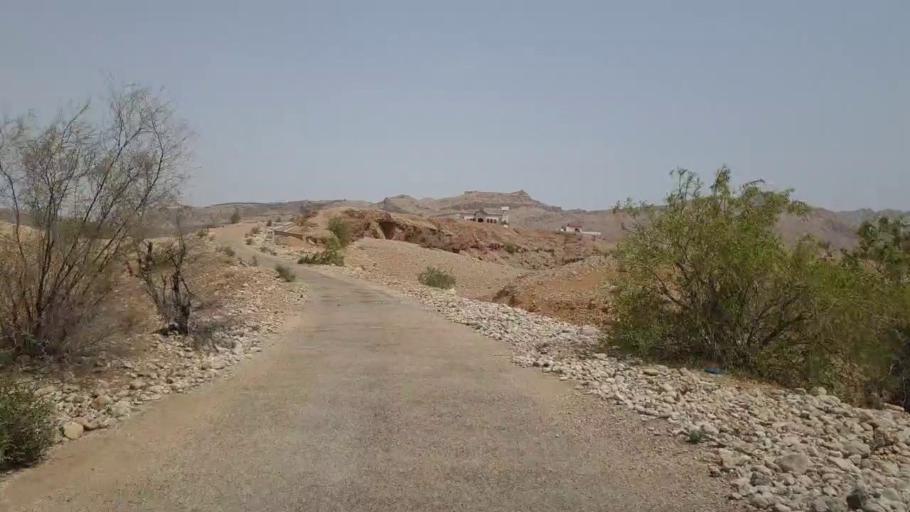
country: PK
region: Sindh
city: Sann
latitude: 25.8931
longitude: 67.9044
